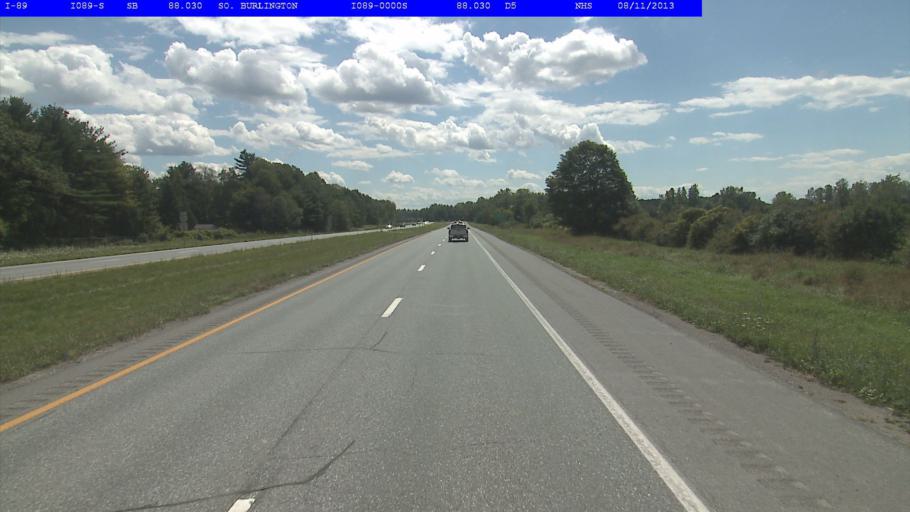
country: US
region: Vermont
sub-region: Chittenden County
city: South Burlington
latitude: 44.4600
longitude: -73.1851
